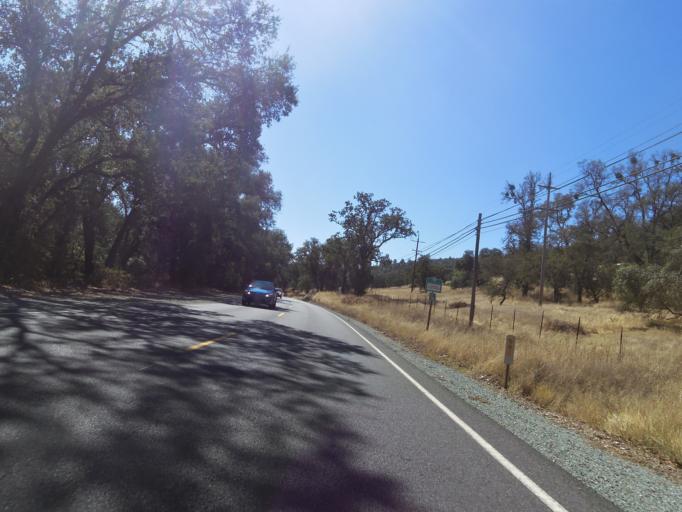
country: US
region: California
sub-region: Amador County
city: Plymouth
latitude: 38.5140
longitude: -120.8488
